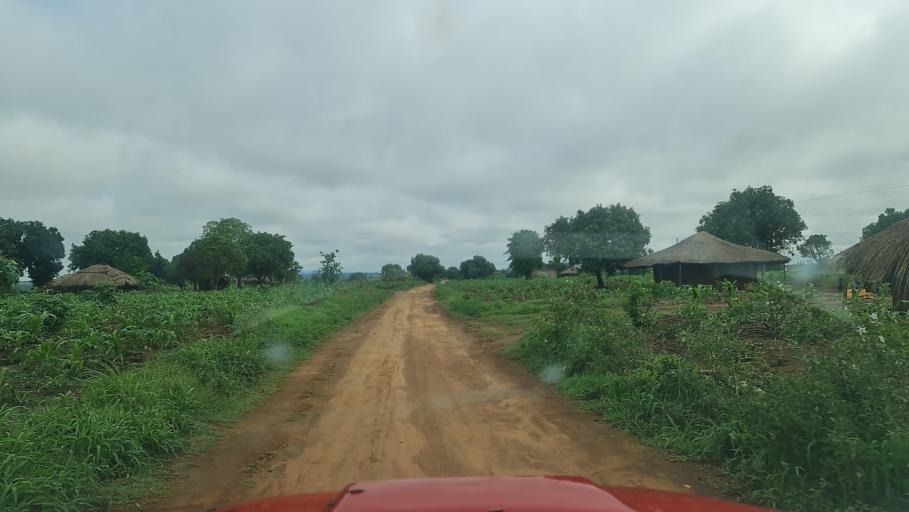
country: MW
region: Southern Region
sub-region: Nsanje District
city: Nsanje
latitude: -17.2116
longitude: 35.6776
